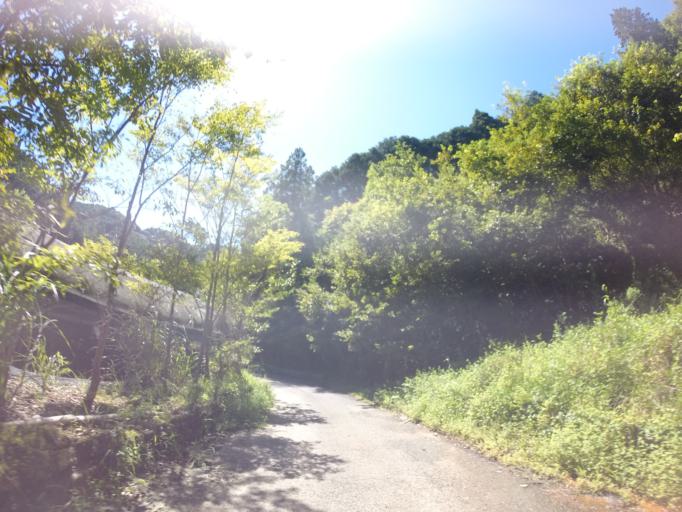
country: JP
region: Shizuoka
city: Shimada
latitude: 34.9100
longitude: 138.1730
